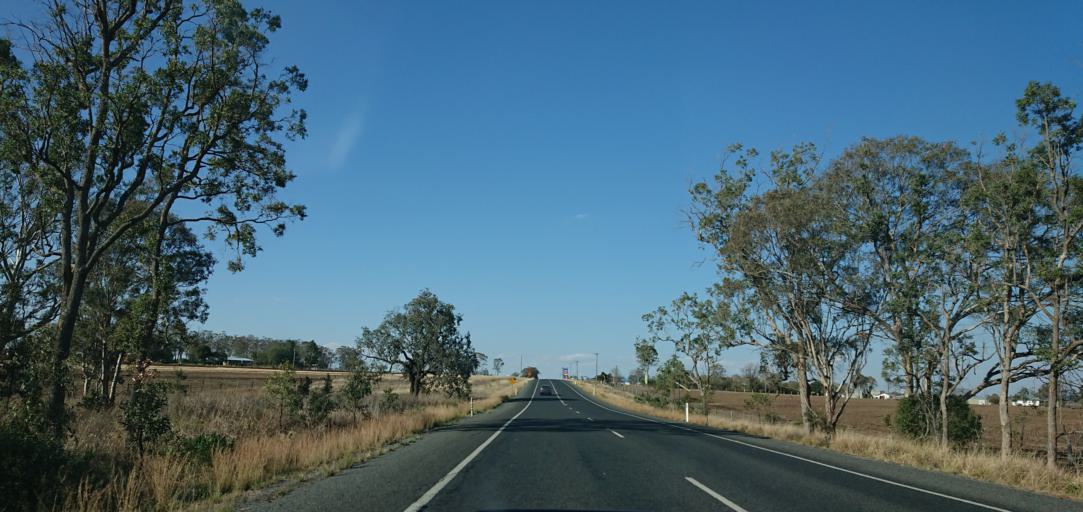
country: AU
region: Queensland
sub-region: Toowoomba
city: Westbrook
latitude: -27.6404
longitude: 151.7379
